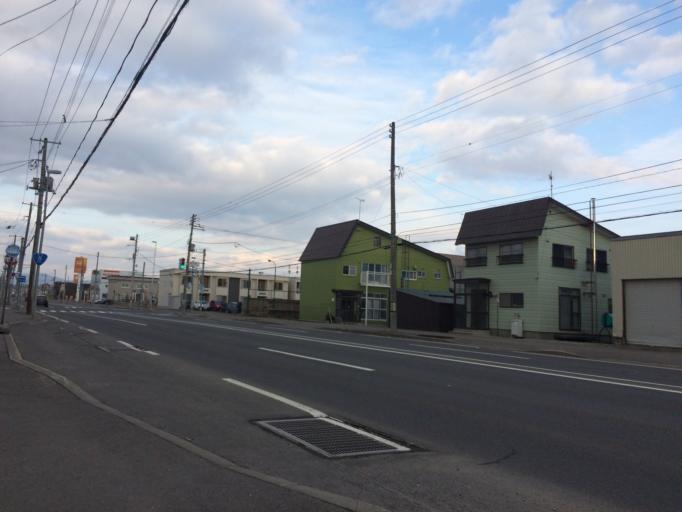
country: JP
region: Hokkaido
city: Niseko Town
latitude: 42.8909
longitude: 140.7516
